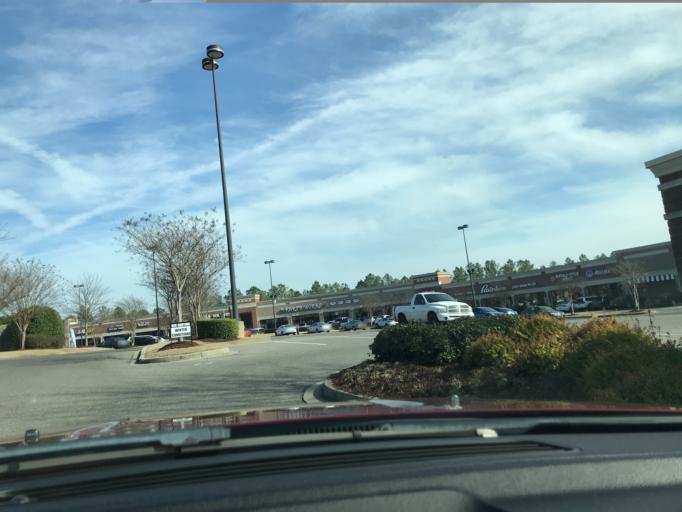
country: US
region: Tennessee
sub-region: Shelby County
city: Germantown
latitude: 35.0483
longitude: -89.8039
